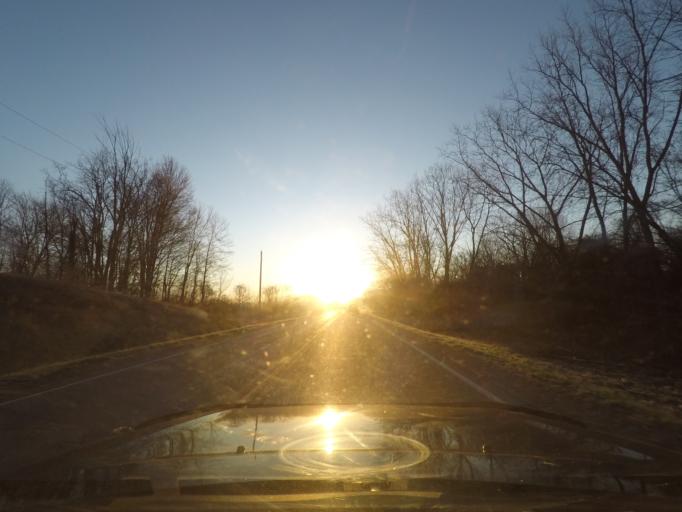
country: US
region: Indiana
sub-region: Marshall County
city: Plymouth
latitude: 41.4491
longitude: -86.3248
